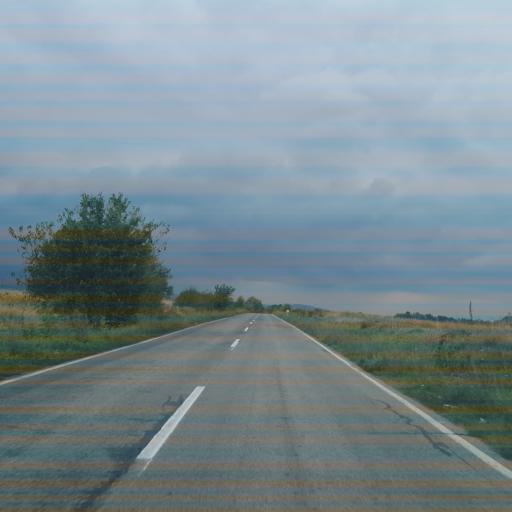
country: RS
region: Central Serbia
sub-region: Nisavski Okrug
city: Razanj
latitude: 43.6041
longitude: 21.6098
